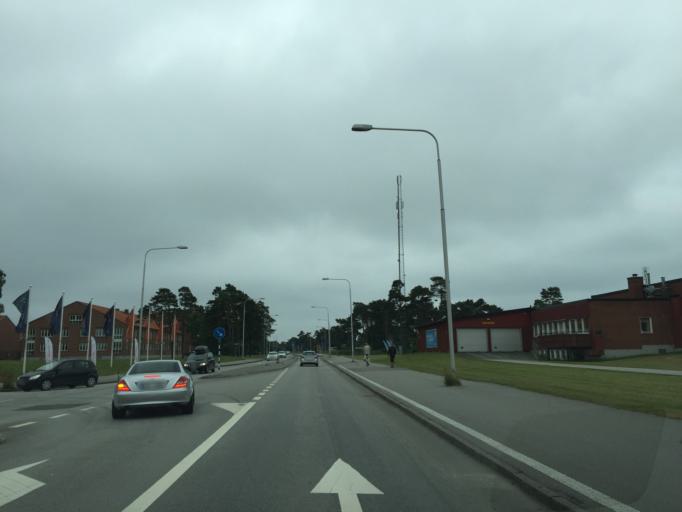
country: SE
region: Skane
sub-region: Ystads Kommun
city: Ystad
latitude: 55.4345
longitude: 13.8383
